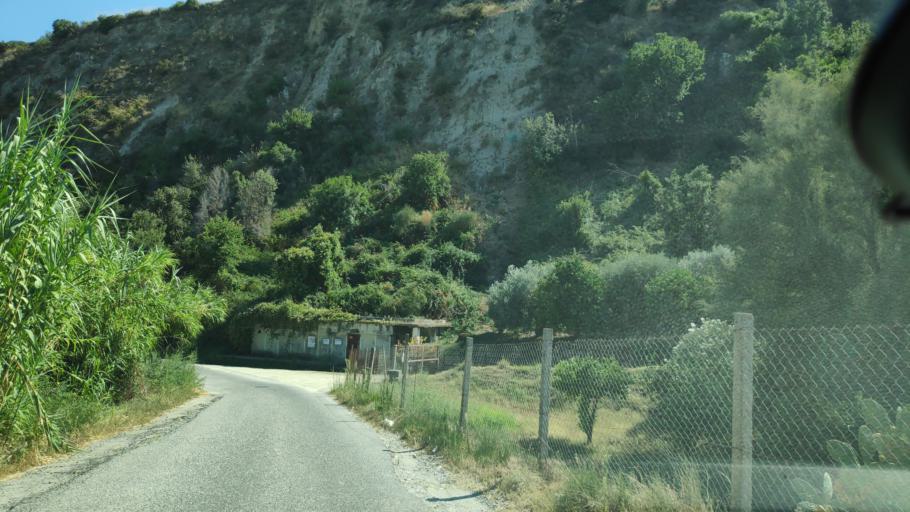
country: IT
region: Calabria
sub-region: Provincia di Reggio Calabria
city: Monasterace
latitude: 38.4423
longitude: 16.5215
